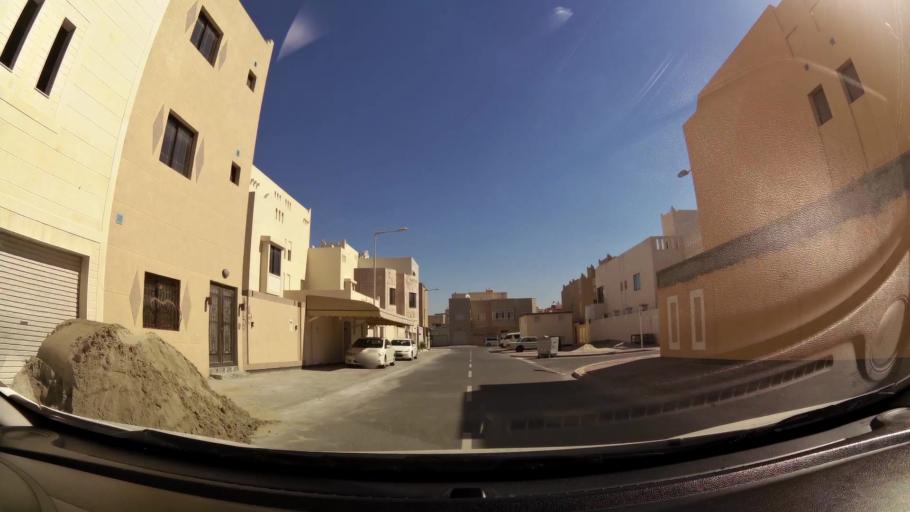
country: BH
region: Muharraq
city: Al Hadd
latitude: 26.2488
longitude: 50.6336
